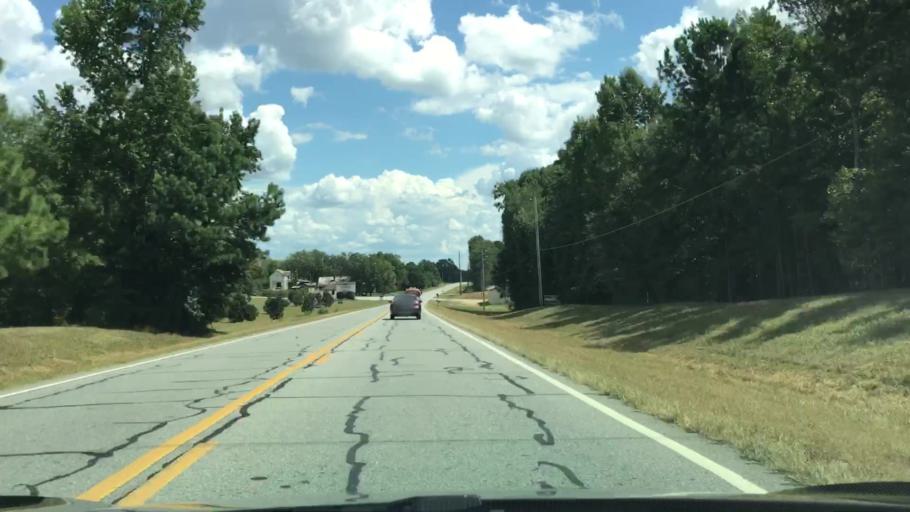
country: US
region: Georgia
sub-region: Oconee County
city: Watkinsville
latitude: 33.8075
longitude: -83.3489
